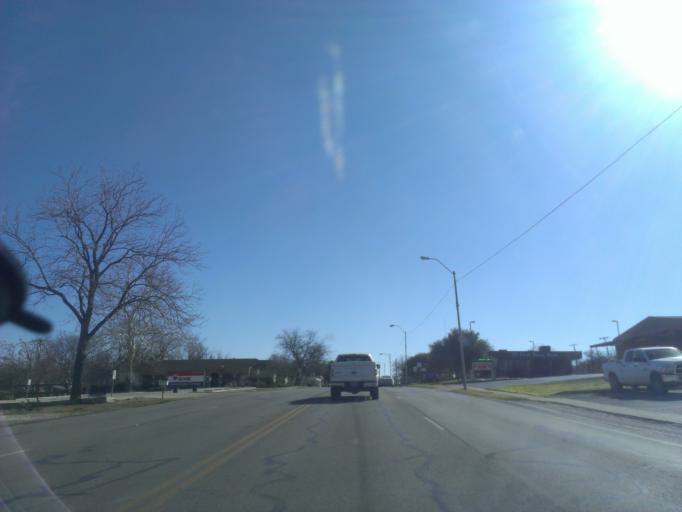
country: US
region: Texas
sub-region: Williamson County
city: Taylor
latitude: 30.5762
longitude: -97.4102
